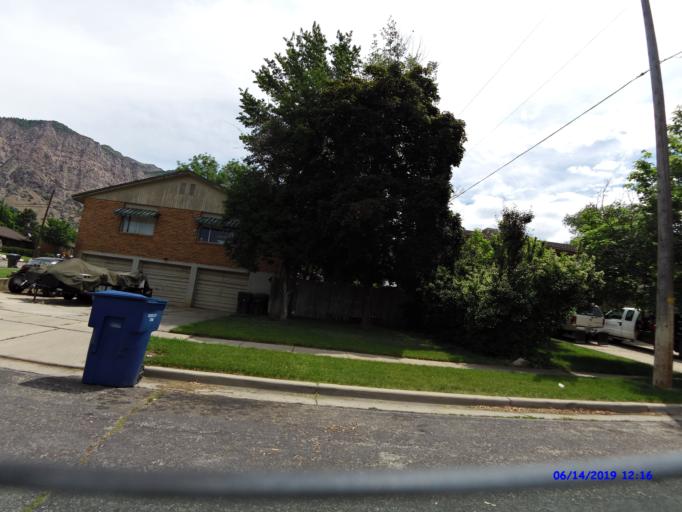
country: US
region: Utah
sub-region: Weber County
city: Ogden
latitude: 41.2547
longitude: -111.9524
